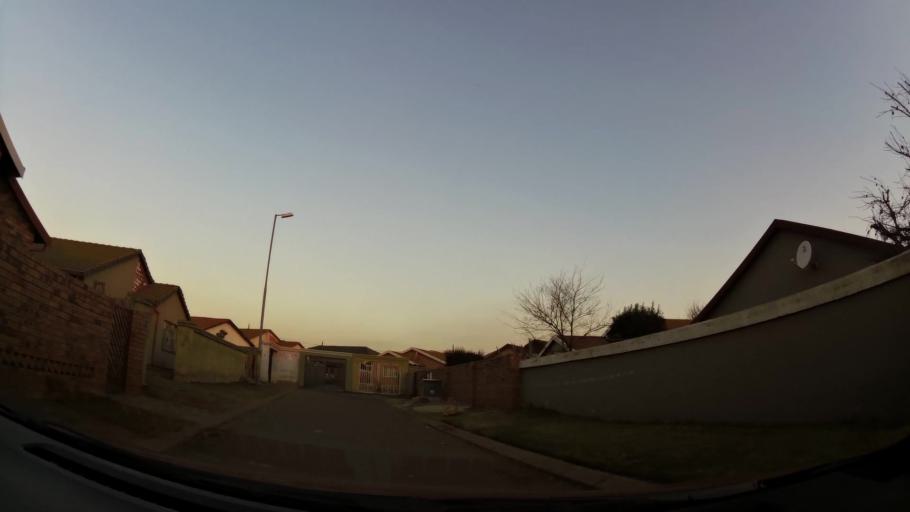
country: ZA
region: Gauteng
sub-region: City of Johannesburg Metropolitan Municipality
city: Soweto
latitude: -26.2268
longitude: 27.8400
